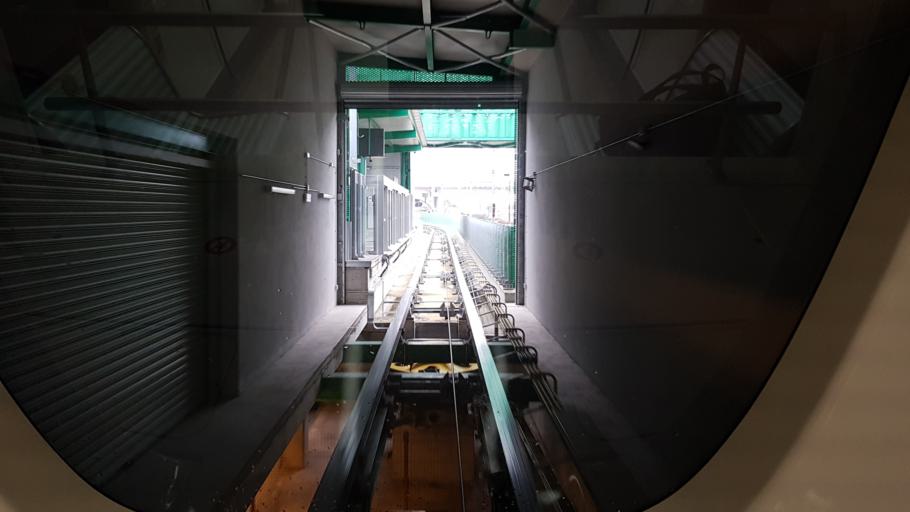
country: IT
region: Tuscany
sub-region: Province of Pisa
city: Pisa
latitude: 43.7014
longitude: 10.3914
